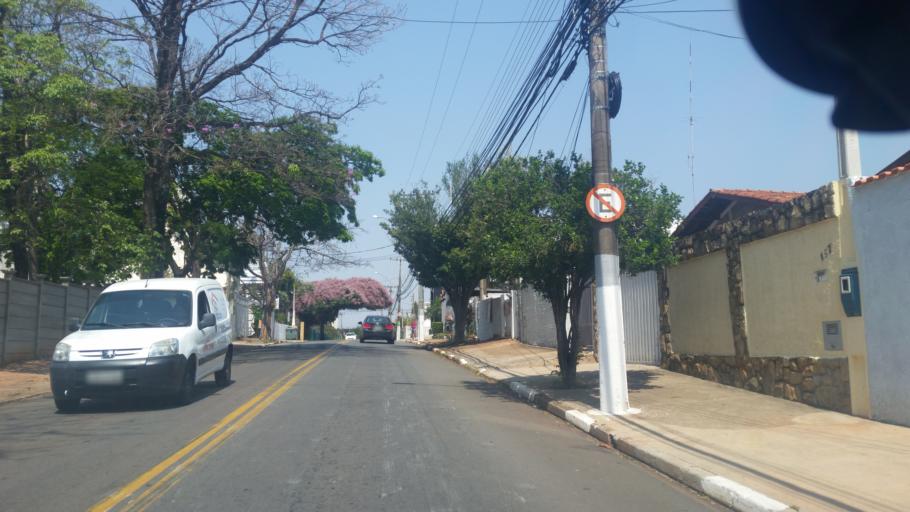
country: BR
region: Sao Paulo
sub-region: Campinas
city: Campinas
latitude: -22.8473
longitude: -47.0532
